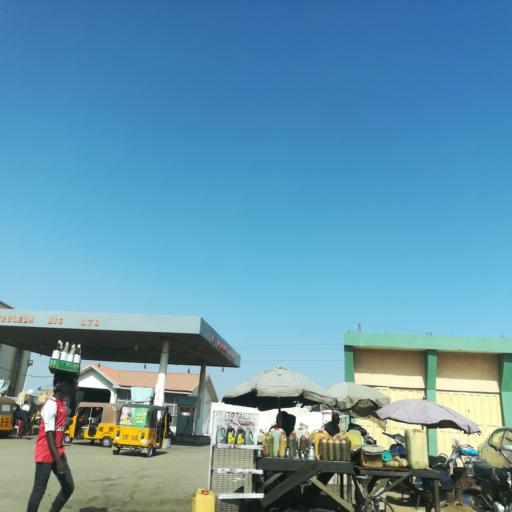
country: NG
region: Kano
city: Kano
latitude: 12.0095
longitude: 8.5237
